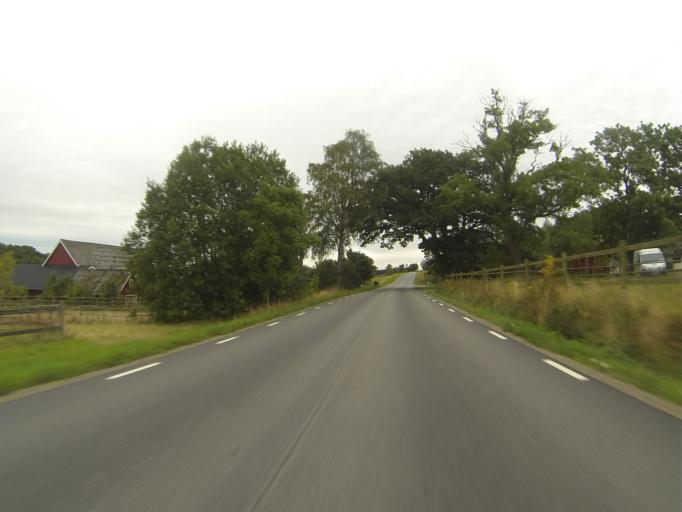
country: SE
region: Skane
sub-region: Lunds Kommun
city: Veberod
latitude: 55.6427
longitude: 13.4294
